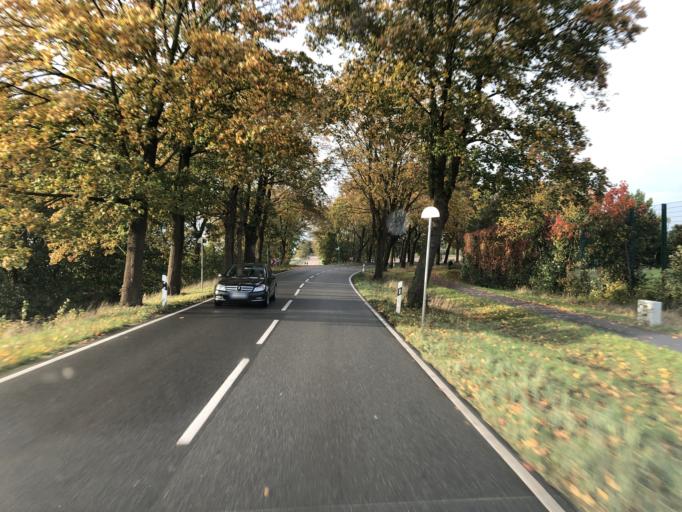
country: DE
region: Lower Saxony
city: Neu Wulmstorf
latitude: 53.4474
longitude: 9.8002
